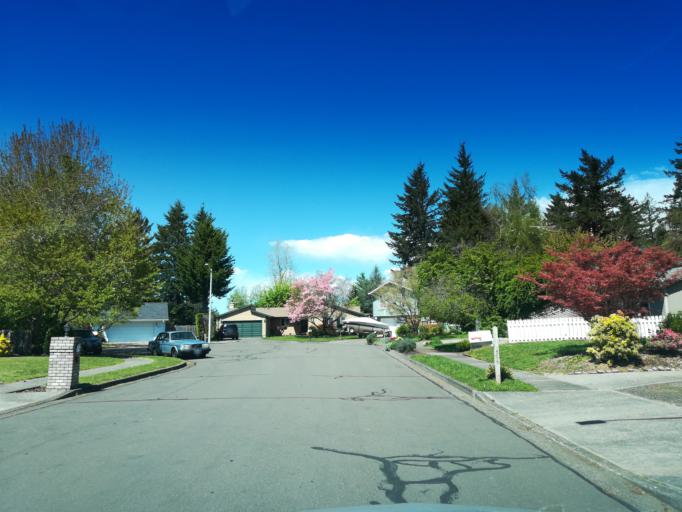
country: US
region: Oregon
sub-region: Multnomah County
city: Troutdale
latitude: 45.5241
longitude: -122.3753
